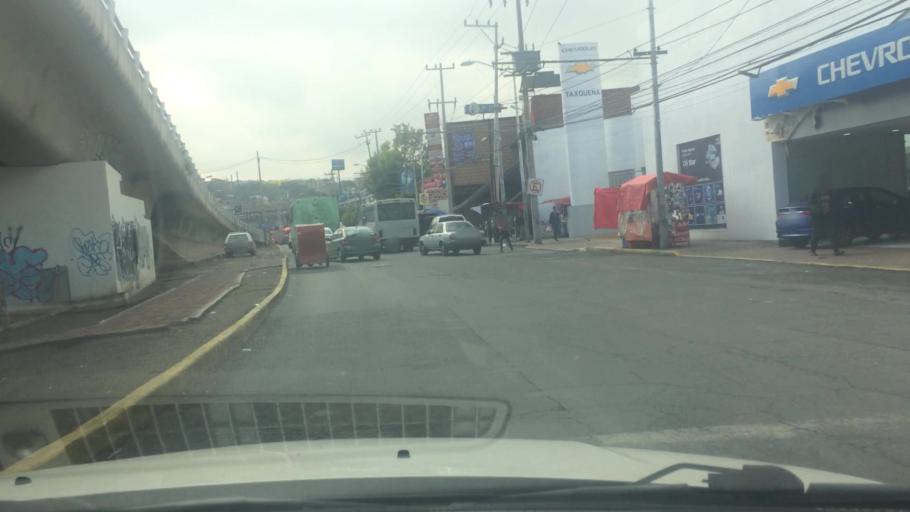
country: MX
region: Mexico City
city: Iztapalapa
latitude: 19.3383
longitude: -99.1110
